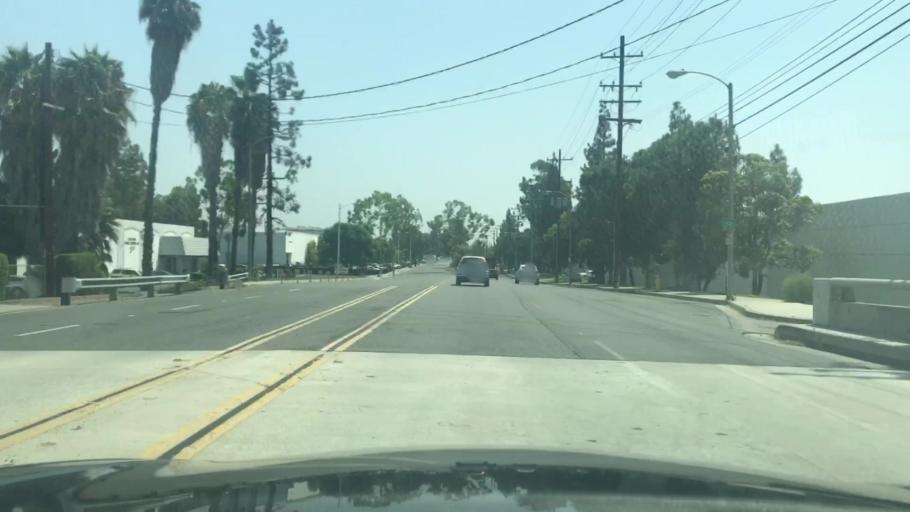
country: US
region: California
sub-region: Orange County
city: La Palma
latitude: 33.8733
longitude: -118.0328
